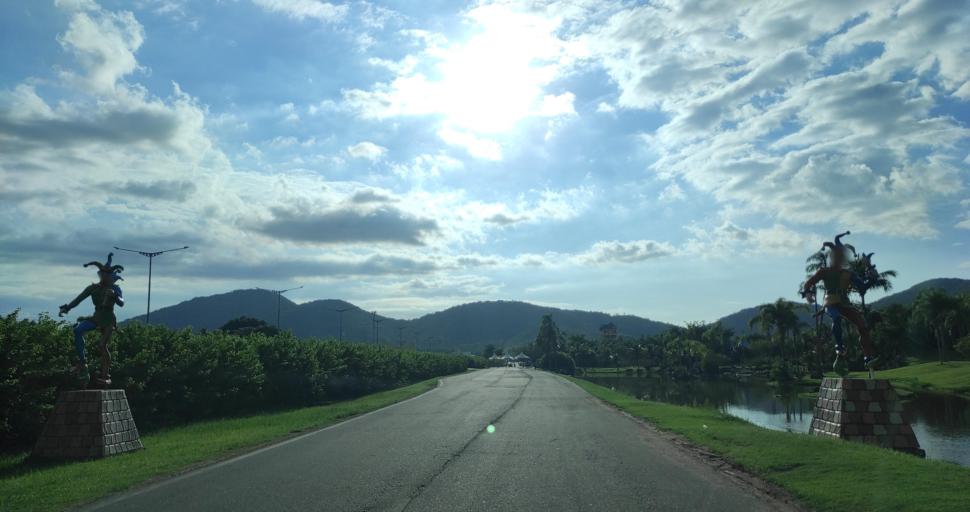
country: BR
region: Santa Catarina
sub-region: Penha
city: Penha
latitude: -26.7984
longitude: -48.6193
